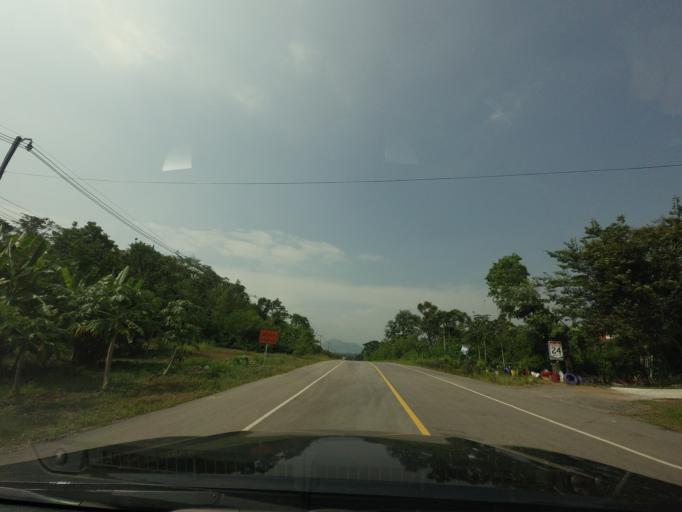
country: LA
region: Xiagnabouli
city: Muang Kenthao
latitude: 17.7154
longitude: 101.4336
